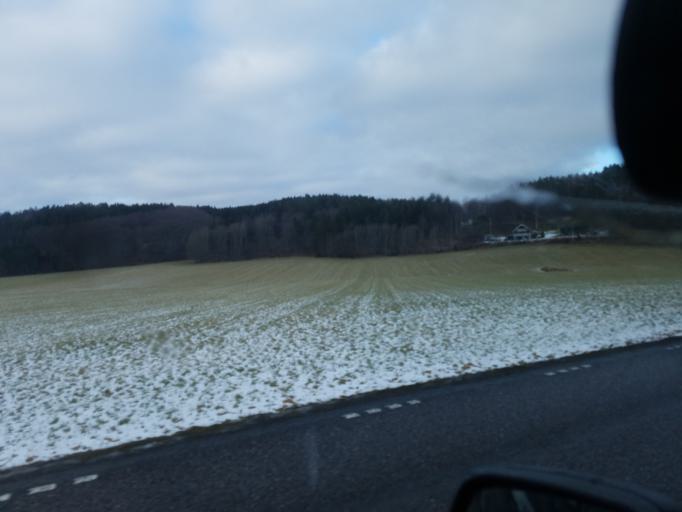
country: SE
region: Vaestra Goetaland
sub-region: Orust
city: Henan
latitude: 58.3335
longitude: 11.6884
